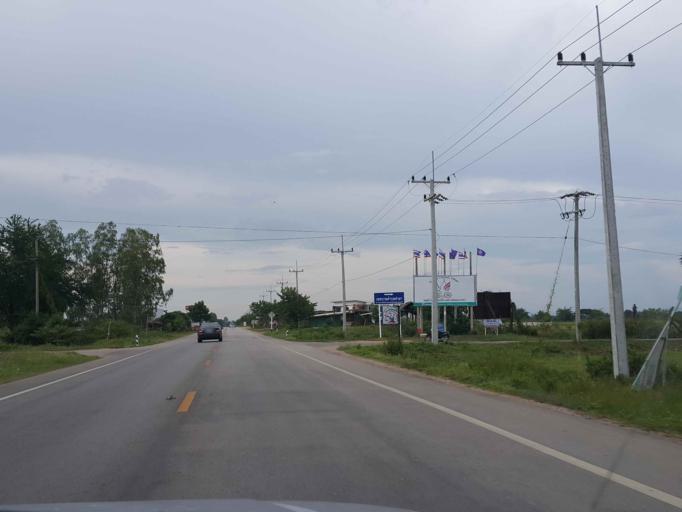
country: TH
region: Lampang
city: Ko Kha
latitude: 18.2113
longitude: 99.3919
